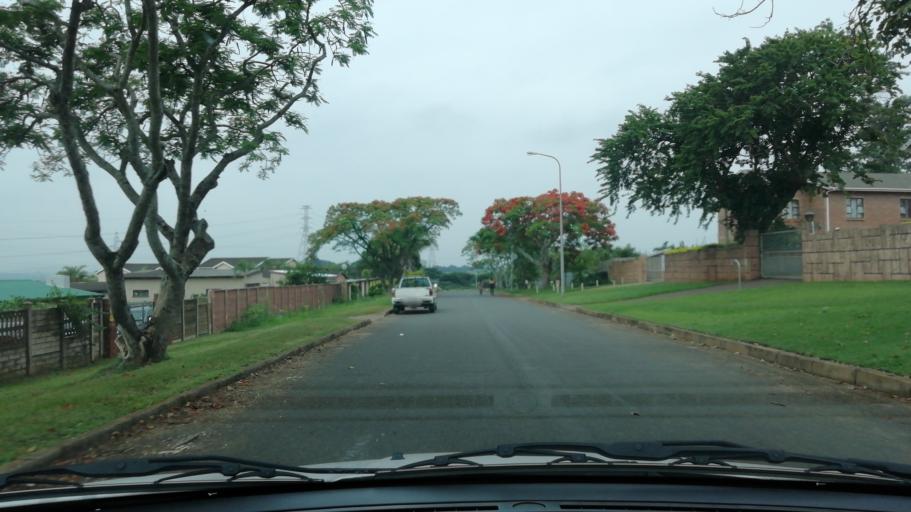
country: ZA
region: KwaZulu-Natal
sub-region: uThungulu District Municipality
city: Empangeni
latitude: -28.7382
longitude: 31.8898
